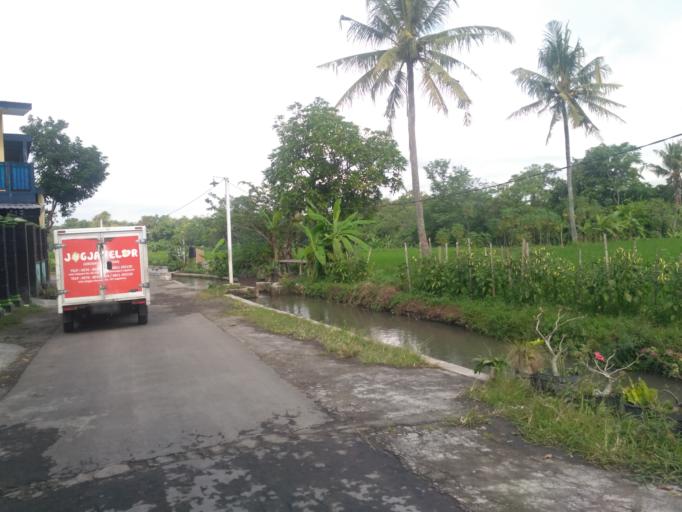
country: ID
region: Daerah Istimewa Yogyakarta
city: Melati
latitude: -7.7538
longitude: 110.3548
